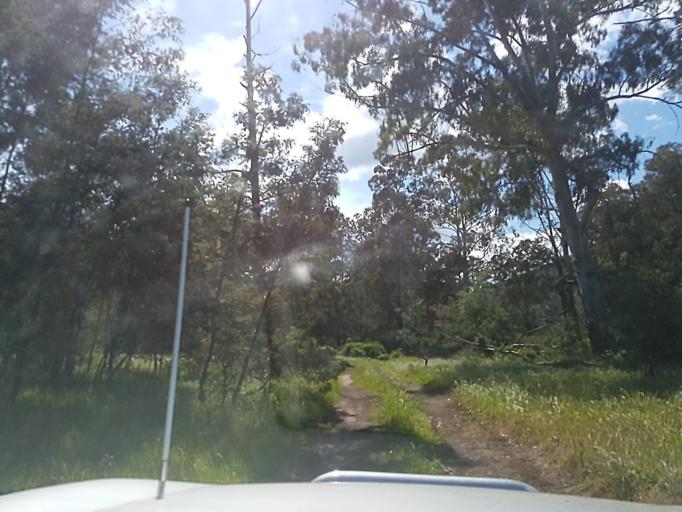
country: AU
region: Victoria
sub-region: Alpine
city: Mount Beauty
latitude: -37.3744
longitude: 147.0317
